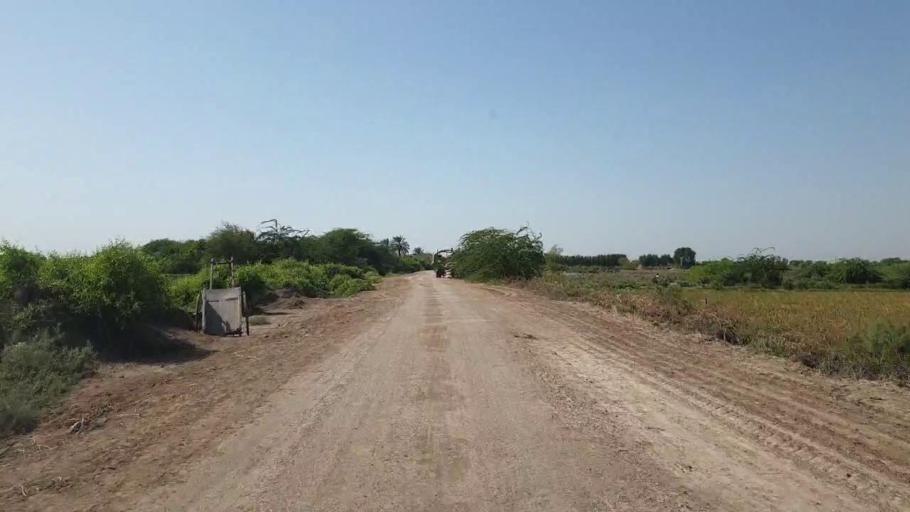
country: PK
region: Sindh
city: Tando Bago
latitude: 24.7048
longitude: 69.0285
